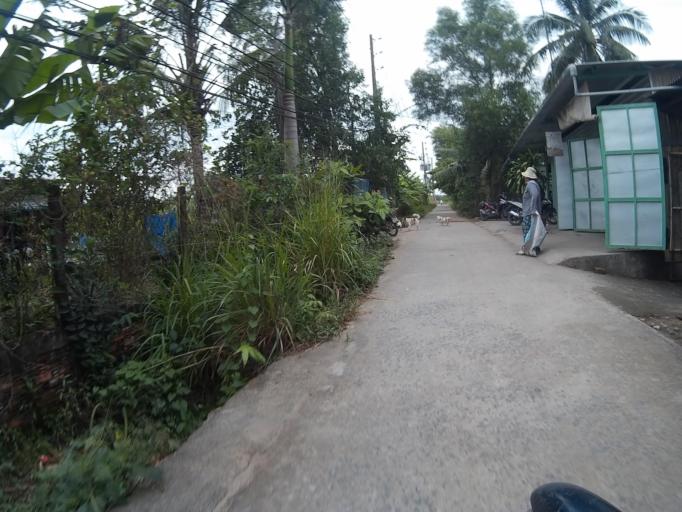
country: VN
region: Ho Chi Minh City
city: Quan Hai
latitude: 10.8167
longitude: 106.7448
